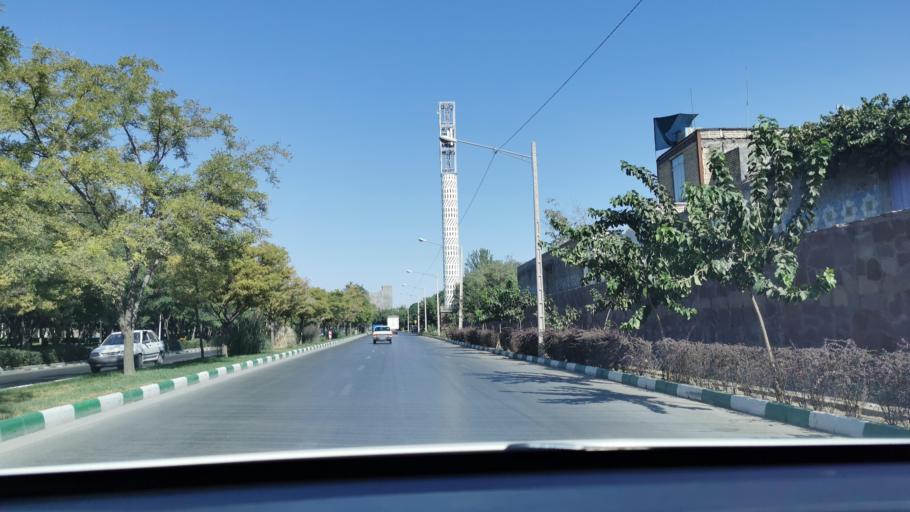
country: IR
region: Razavi Khorasan
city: Mashhad
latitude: 36.3336
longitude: 59.6366
